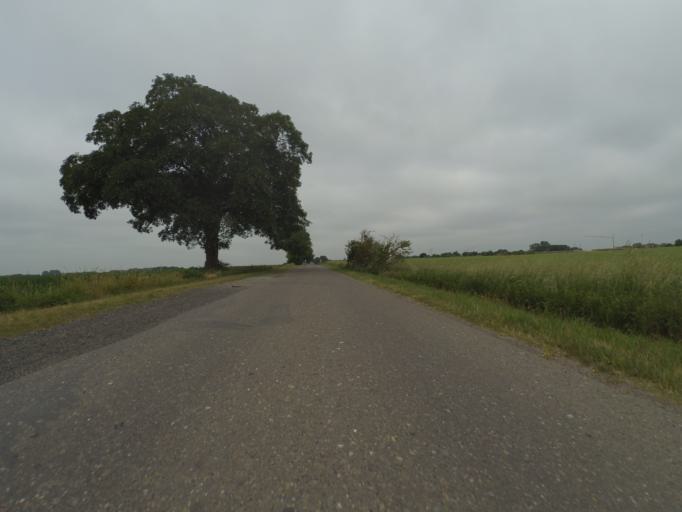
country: DE
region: Mecklenburg-Vorpommern
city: Plau am See
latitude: 53.4649
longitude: 12.2558
